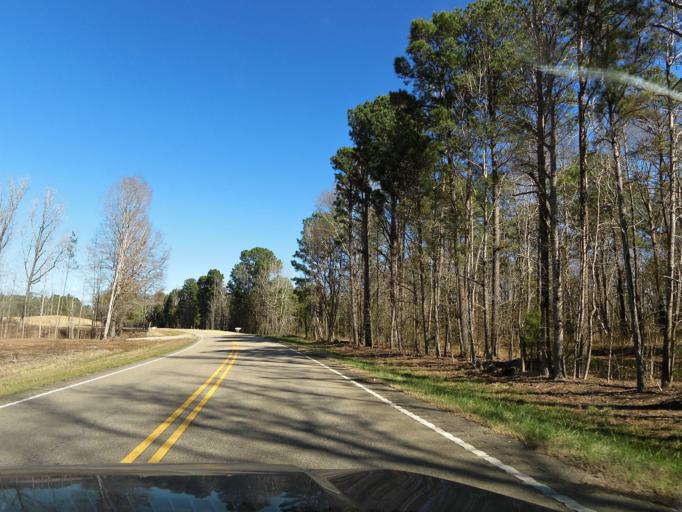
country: US
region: Alabama
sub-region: Bullock County
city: Union Springs
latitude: 32.1261
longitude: -85.7717
